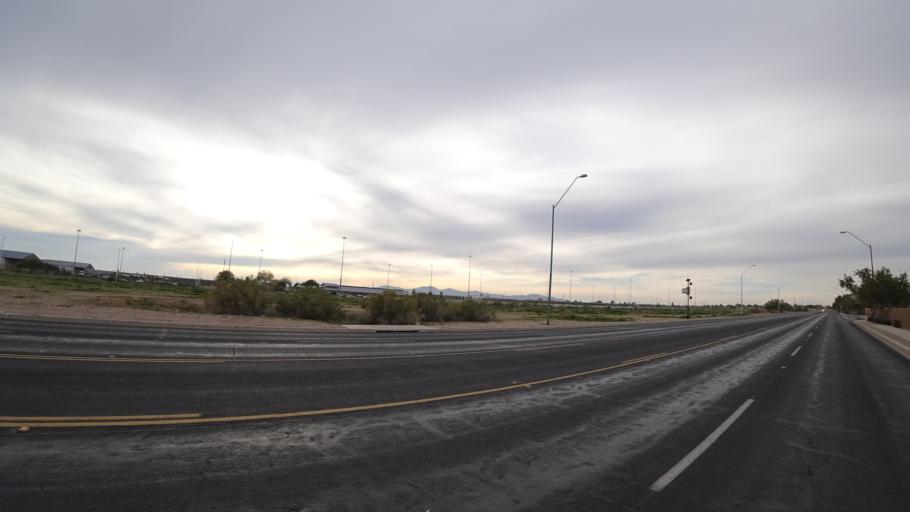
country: US
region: Arizona
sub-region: Maricopa County
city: El Mirage
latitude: 33.6176
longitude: -112.3154
